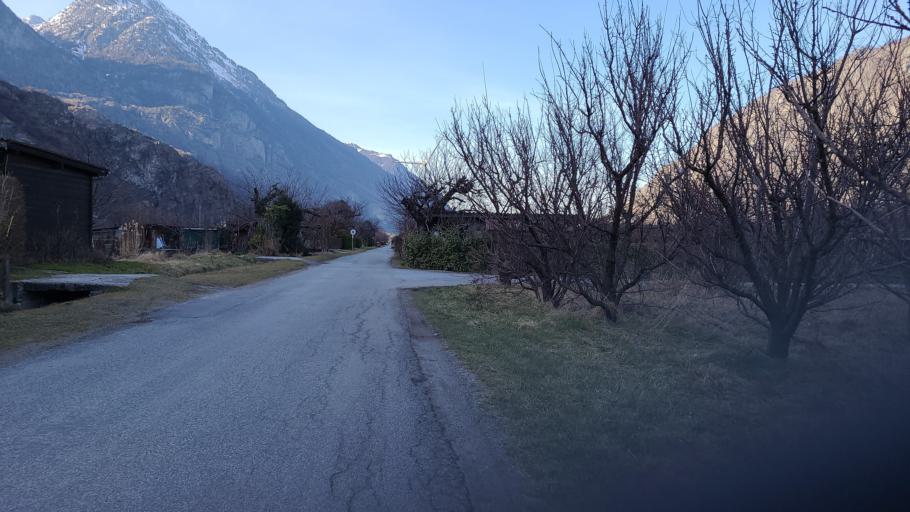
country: CH
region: Valais
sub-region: Martigny District
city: Martigny-Ville
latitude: 46.1204
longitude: 7.0580
